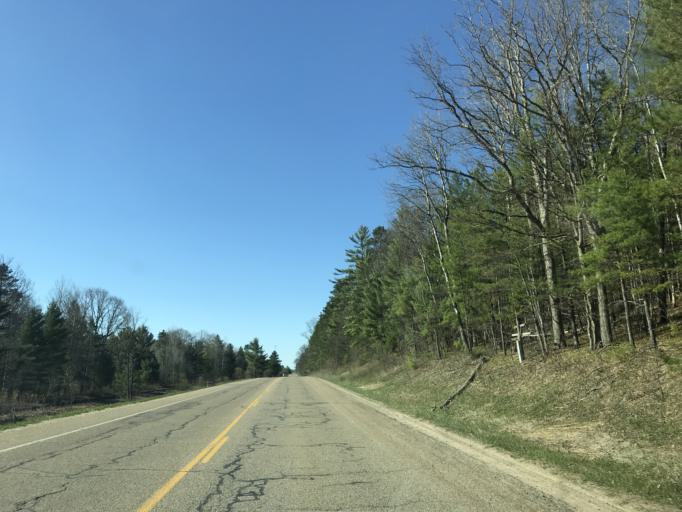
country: US
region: Michigan
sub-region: Crawford County
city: Grayling
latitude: 44.7233
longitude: -84.7473
